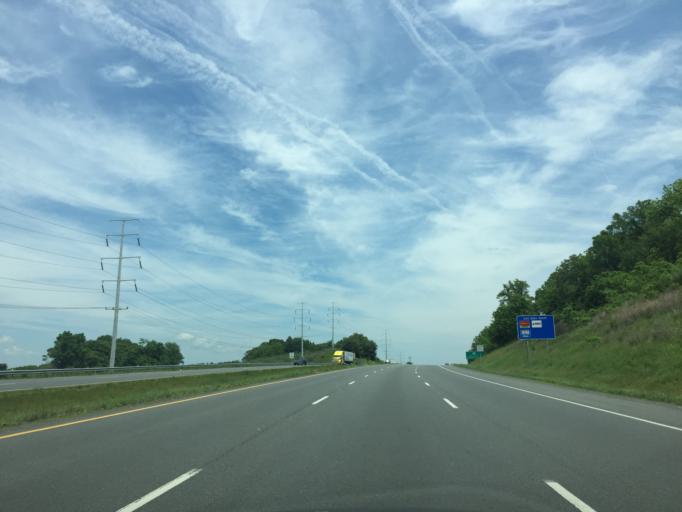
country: US
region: Virginia
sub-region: City of Winchester
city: Winchester
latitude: 39.2055
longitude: -78.1879
